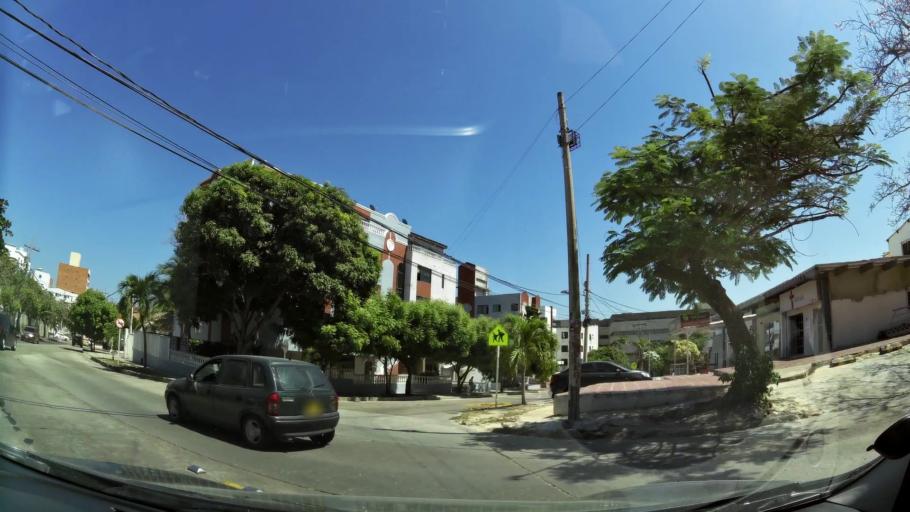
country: CO
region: Atlantico
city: Barranquilla
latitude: 10.9931
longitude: -74.8149
